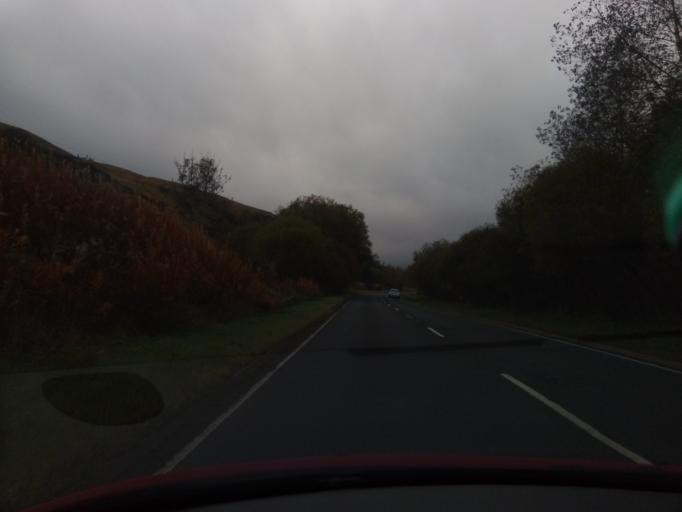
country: GB
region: Scotland
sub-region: The Scottish Borders
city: Galashiels
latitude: 55.6254
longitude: -2.8598
